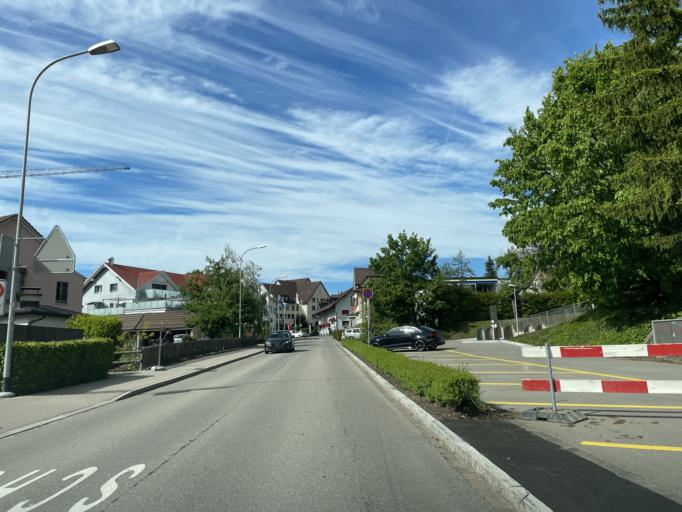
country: CH
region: Zurich
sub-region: Bezirk Uster
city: Bruttisellen
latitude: 47.4221
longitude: 8.6298
